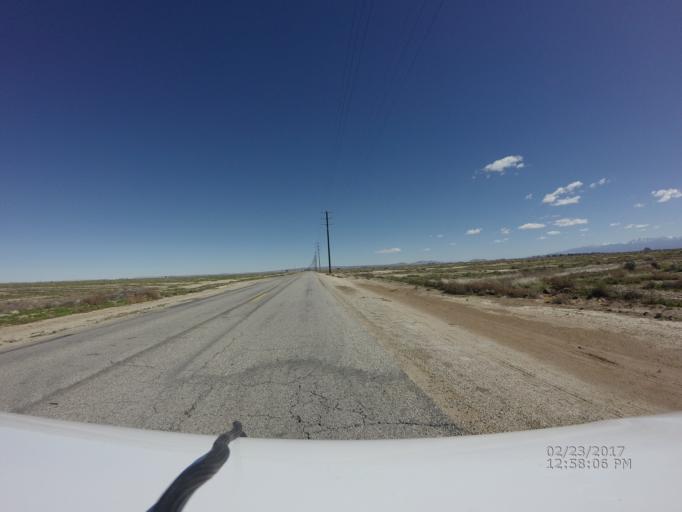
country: US
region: California
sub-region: Los Angeles County
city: Lancaster
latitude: 34.7630
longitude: -118.0463
